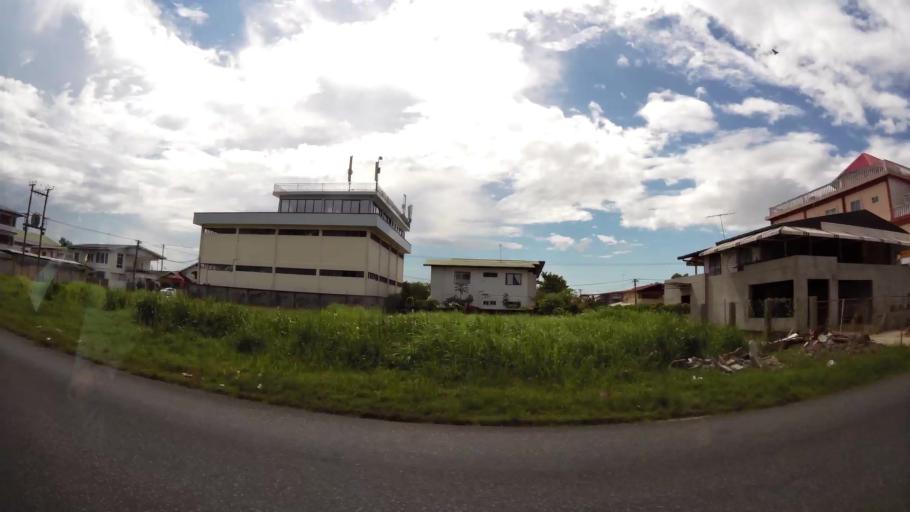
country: SR
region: Paramaribo
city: Paramaribo
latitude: 5.8454
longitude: -55.1420
